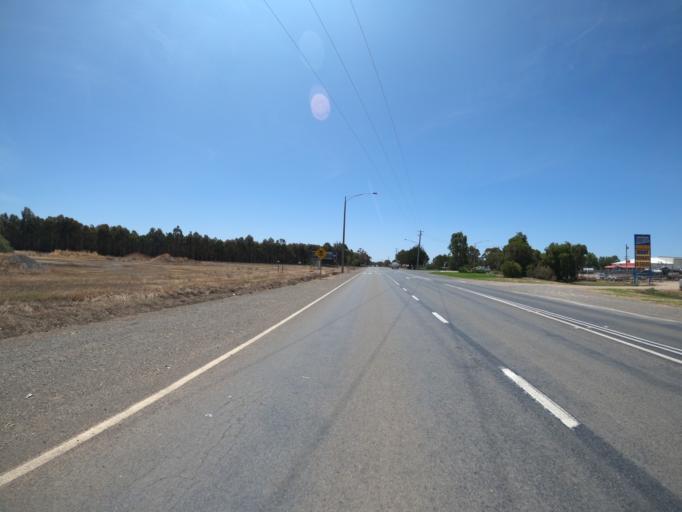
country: AU
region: Victoria
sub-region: Moira
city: Yarrawonga
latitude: -36.0275
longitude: 145.9955
